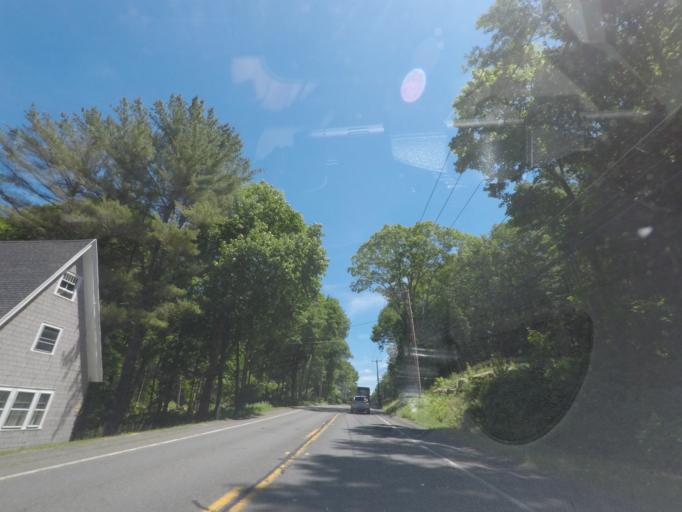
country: US
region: Massachusetts
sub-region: Berkshire County
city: Lee
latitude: 42.2979
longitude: -73.1959
